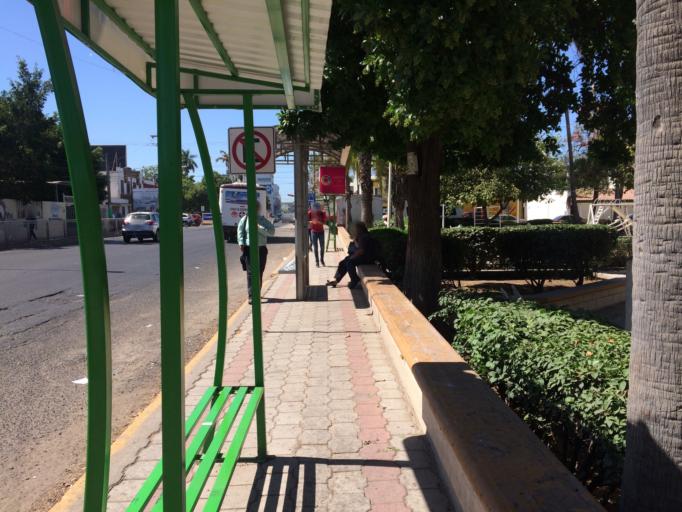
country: MX
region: Sinaloa
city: Culiacan
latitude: 24.8175
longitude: -107.3962
